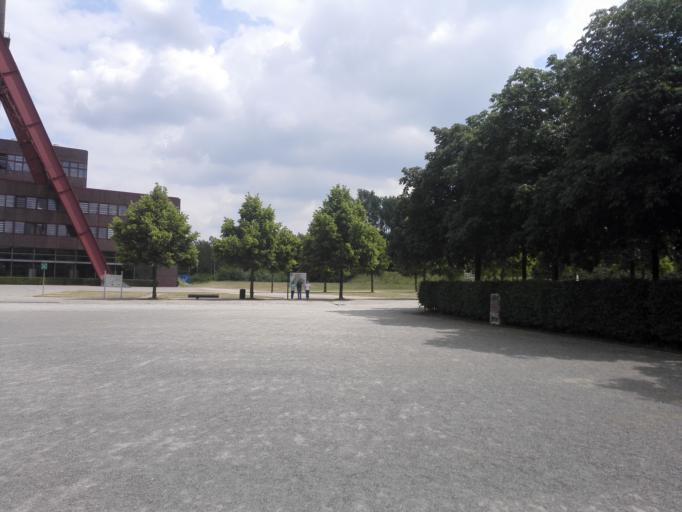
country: DE
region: North Rhine-Westphalia
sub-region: Regierungsbezirk Munster
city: Gladbeck
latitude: 51.5276
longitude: 7.0300
